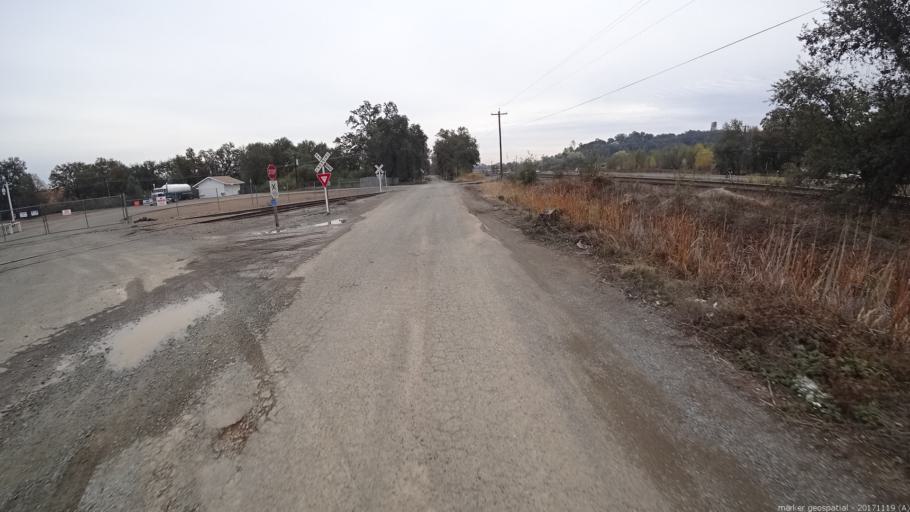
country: US
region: California
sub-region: Shasta County
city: Anderson
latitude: 40.4803
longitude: -122.3441
